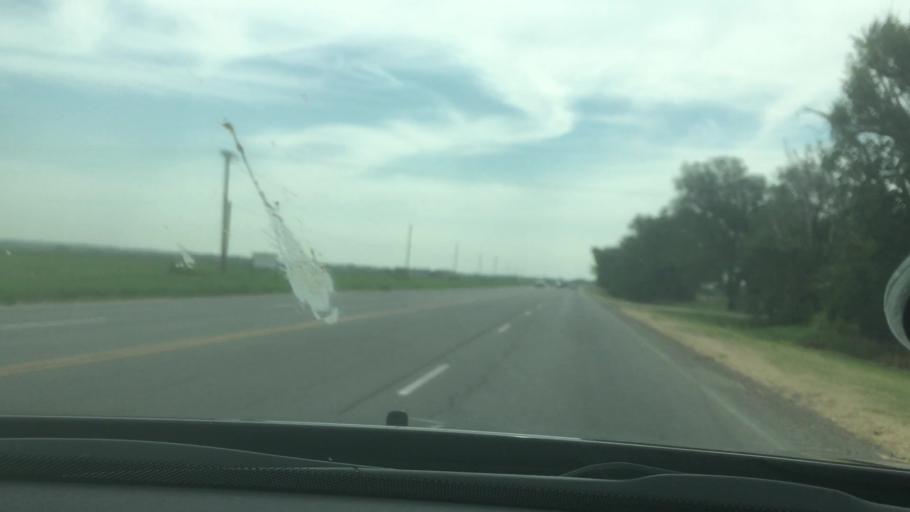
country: US
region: Oklahoma
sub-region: Garvin County
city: Lindsay
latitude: 34.8364
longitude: -97.5939
